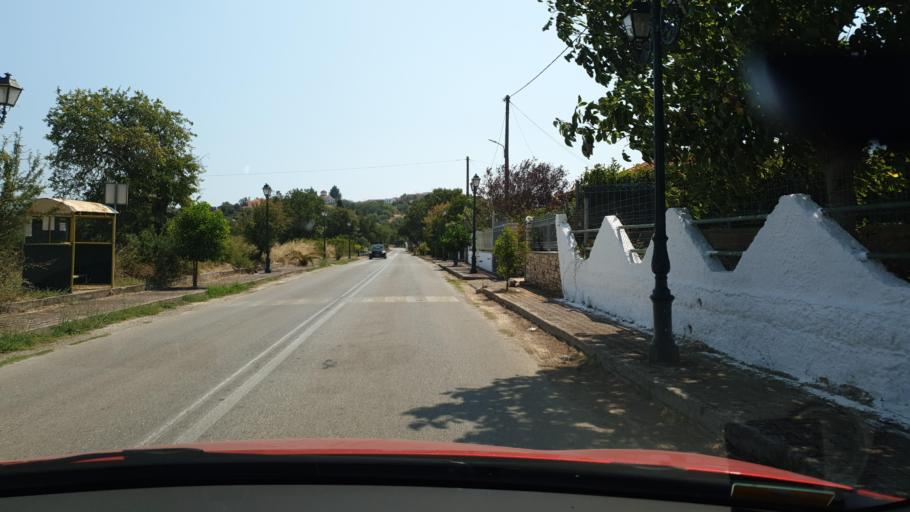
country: GR
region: Central Greece
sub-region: Nomos Evvoias
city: Oxilithos
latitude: 38.5396
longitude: 24.0764
